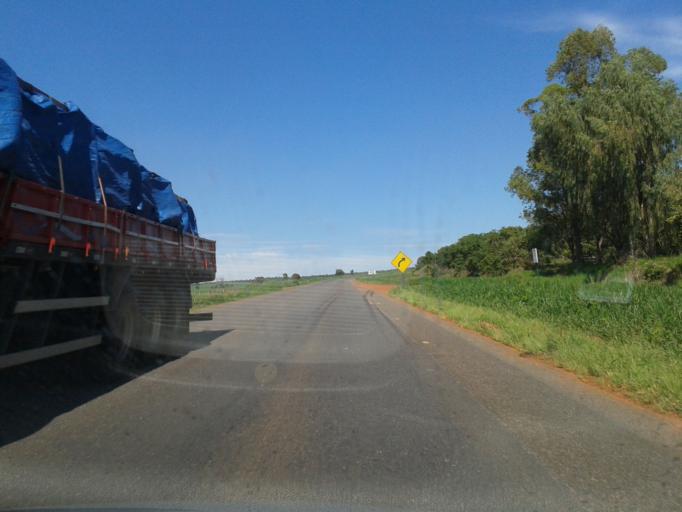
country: BR
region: Goias
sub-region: Bela Vista De Goias
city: Bela Vista de Goias
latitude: -17.1641
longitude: -48.7769
